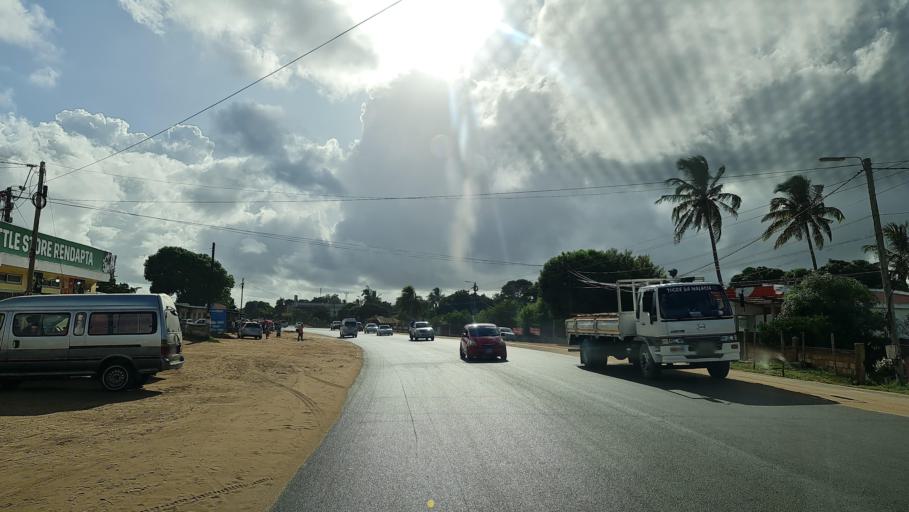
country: MZ
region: Gaza
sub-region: Xai-Xai District
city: Xai-Xai
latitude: -25.0569
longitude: 33.6631
